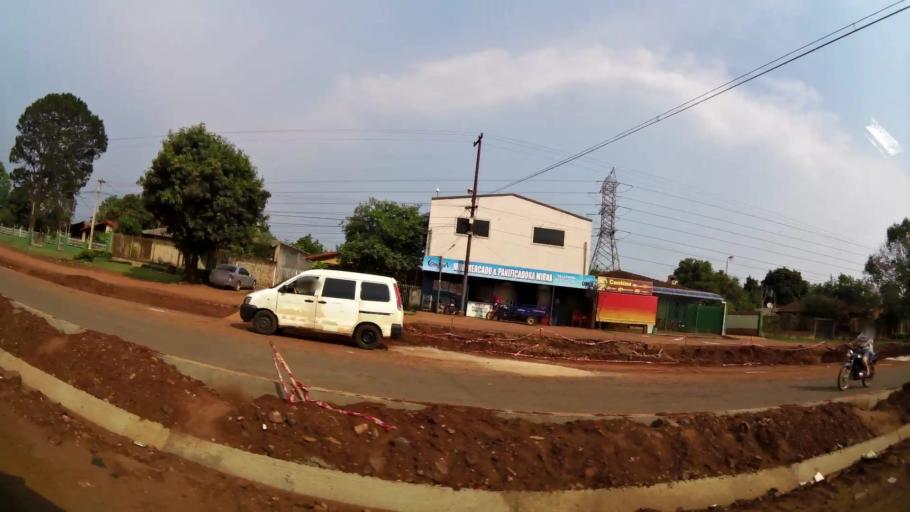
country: PY
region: Alto Parana
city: Ciudad del Este
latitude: -25.4712
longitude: -54.6452
